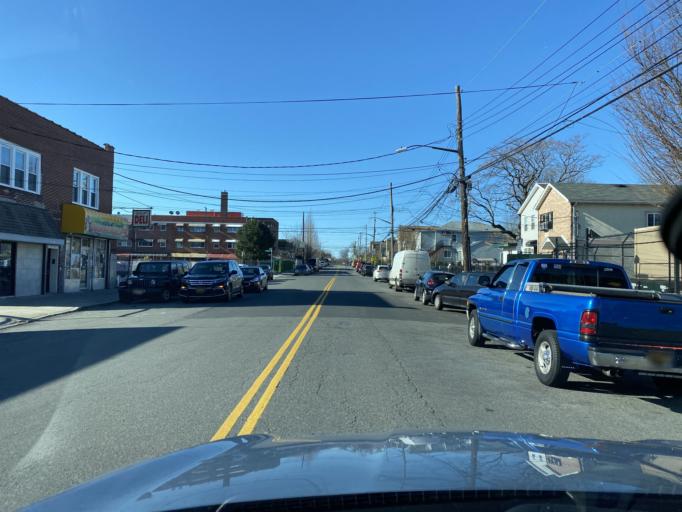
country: US
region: New York
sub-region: Bronx
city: The Bronx
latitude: 40.8176
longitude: -73.8583
